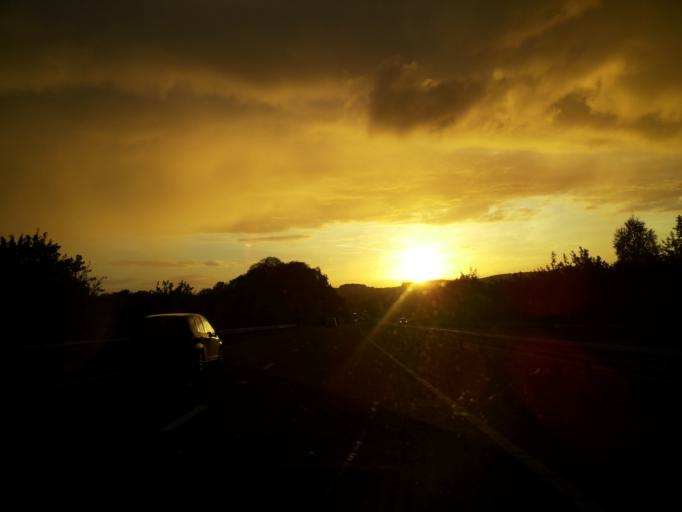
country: GB
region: England
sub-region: Wiltshire
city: Tidworth
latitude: 51.1939
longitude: -1.6550
